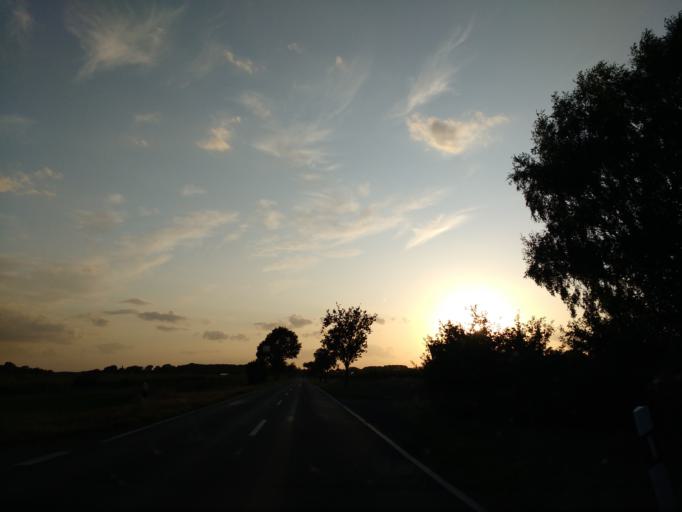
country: DE
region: Lower Saxony
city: Linsburg
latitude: 52.5340
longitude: 9.3500
